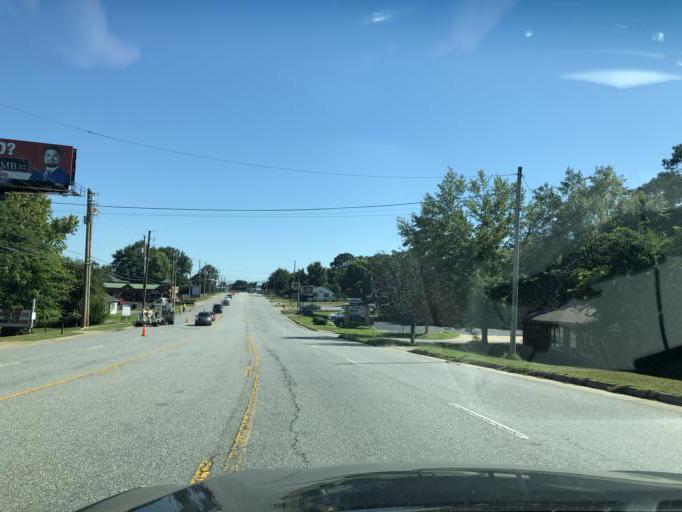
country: US
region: Georgia
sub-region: Muscogee County
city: Columbus
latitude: 32.5127
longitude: -84.9539
